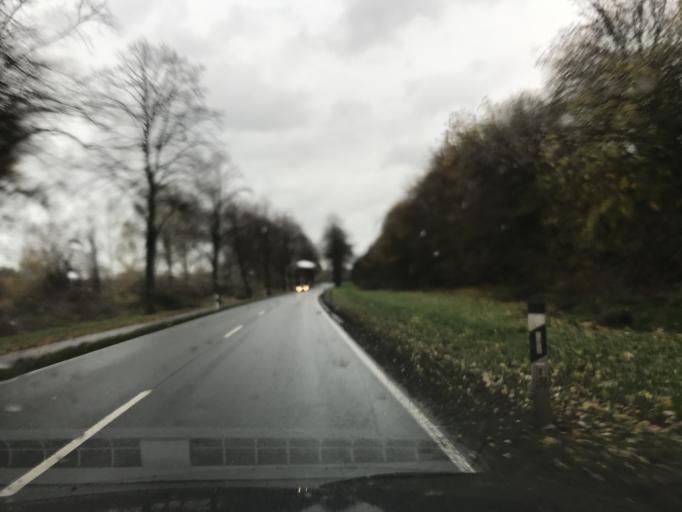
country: DE
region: North Rhine-Westphalia
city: Oelde
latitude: 51.8332
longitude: 8.1650
